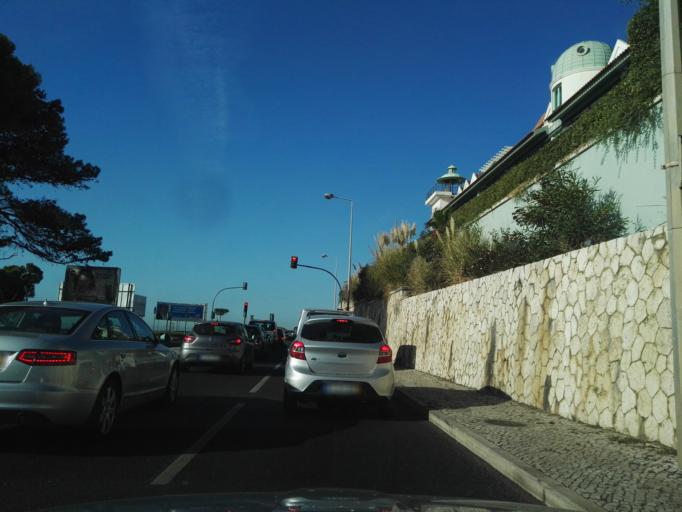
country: PT
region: Lisbon
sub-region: Oeiras
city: Terrugem
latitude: 38.6983
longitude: -9.2824
